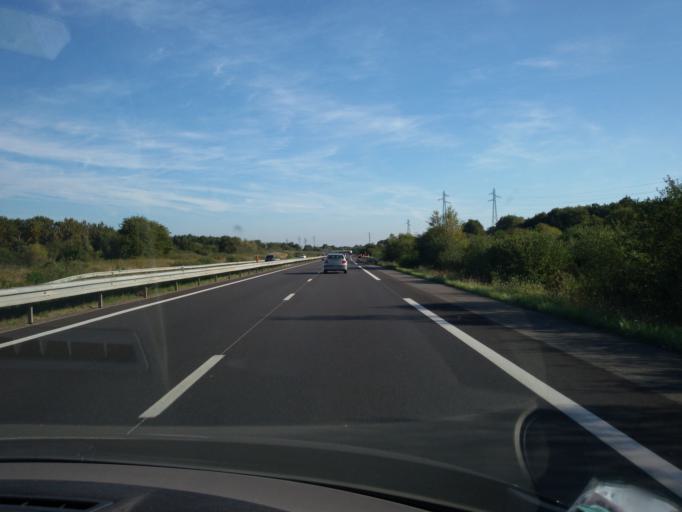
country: FR
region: Centre
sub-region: Departement du Loir-et-Cher
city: Theillay
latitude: 47.3025
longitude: 2.0463
